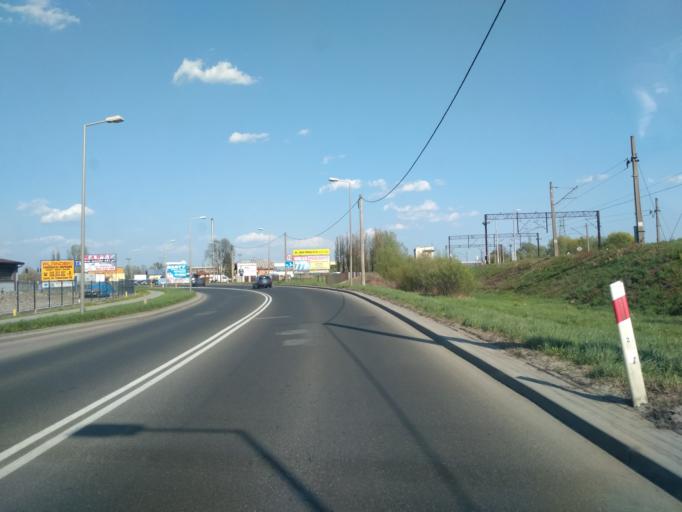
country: PL
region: Subcarpathian Voivodeship
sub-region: Powiat jasielski
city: Jaslo
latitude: 49.7465
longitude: 21.4941
